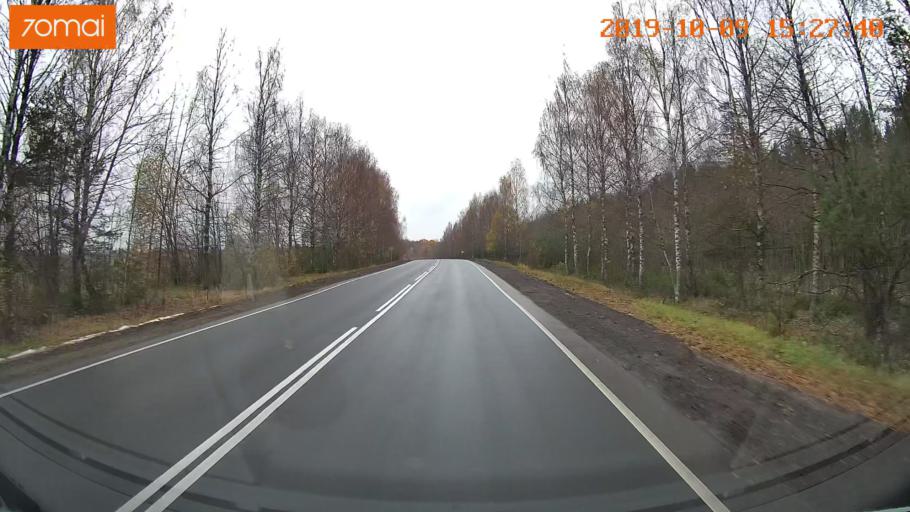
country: RU
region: Kostroma
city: Susanino
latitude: 58.0116
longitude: 41.3742
